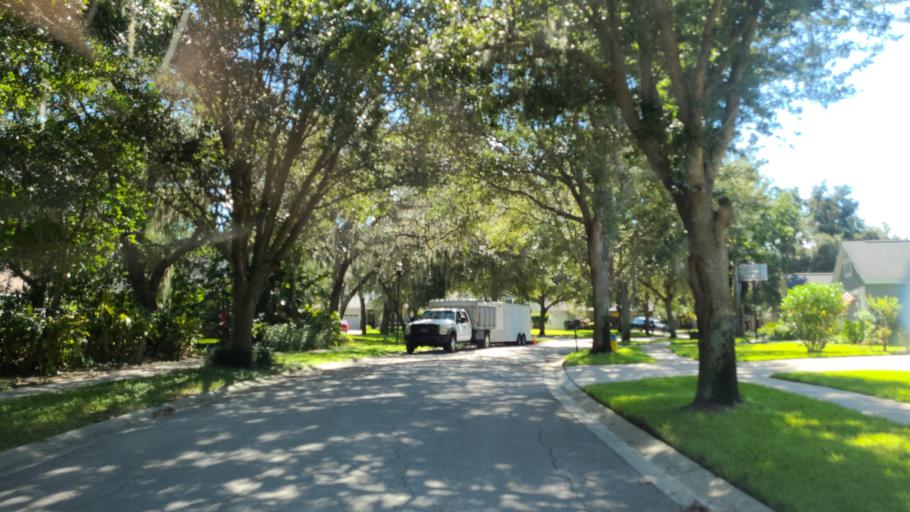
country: US
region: Florida
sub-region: Hillsborough County
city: Fish Hawk
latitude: 27.8409
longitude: -82.2263
